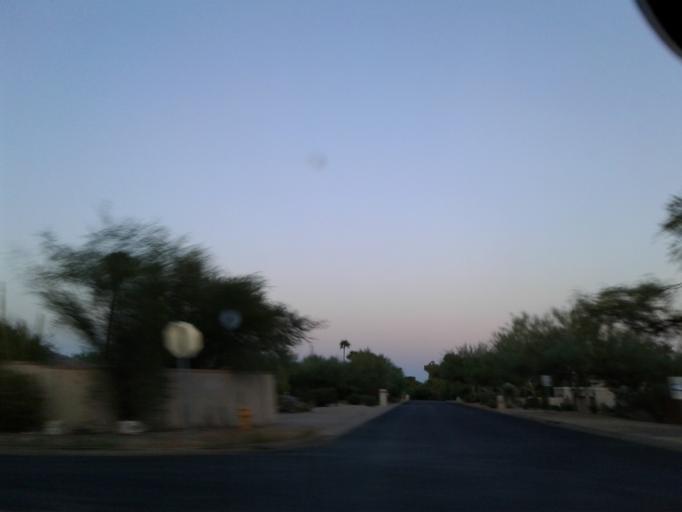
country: US
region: Arizona
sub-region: Maricopa County
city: Paradise Valley
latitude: 33.5718
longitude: -111.9777
